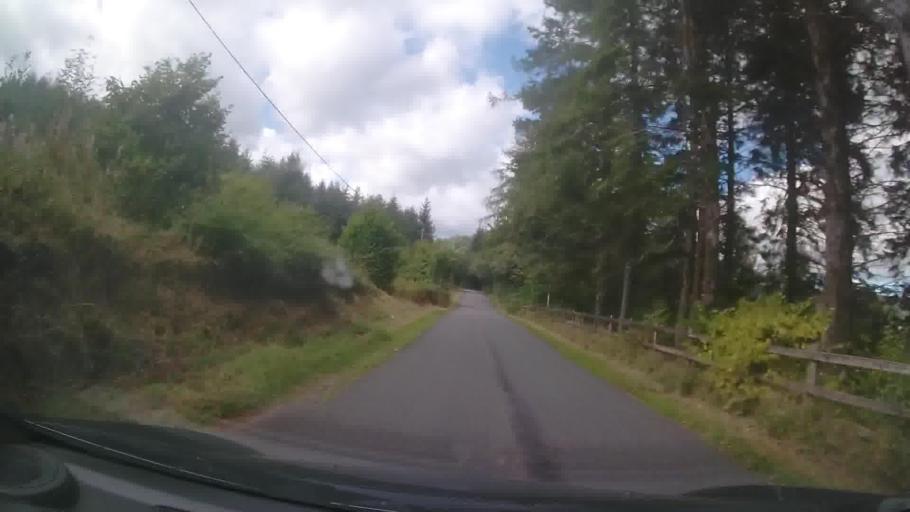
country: GB
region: Wales
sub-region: Merthyr Tydfil County Borough
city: Merthyr Tydfil
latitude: 51.8086
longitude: -3.3744
